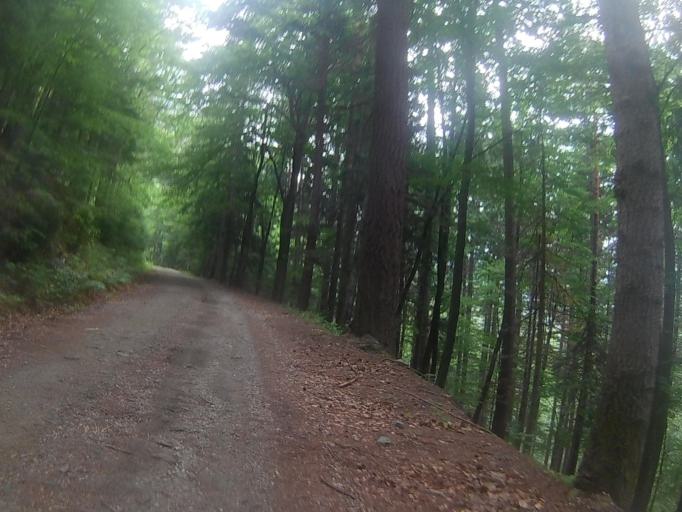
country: SI
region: Ruse
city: Ruse
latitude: 46.5205
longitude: 15.5372
